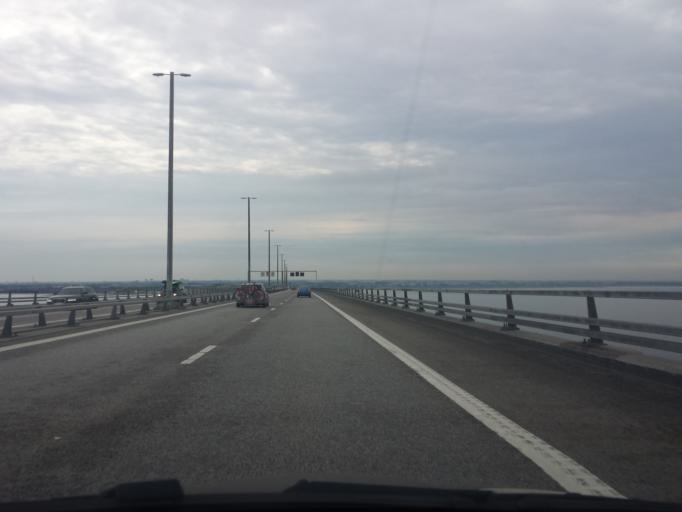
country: SE
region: Skane
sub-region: Malmo
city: Bunkeflostrand
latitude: 55.5704
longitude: 12.8496
